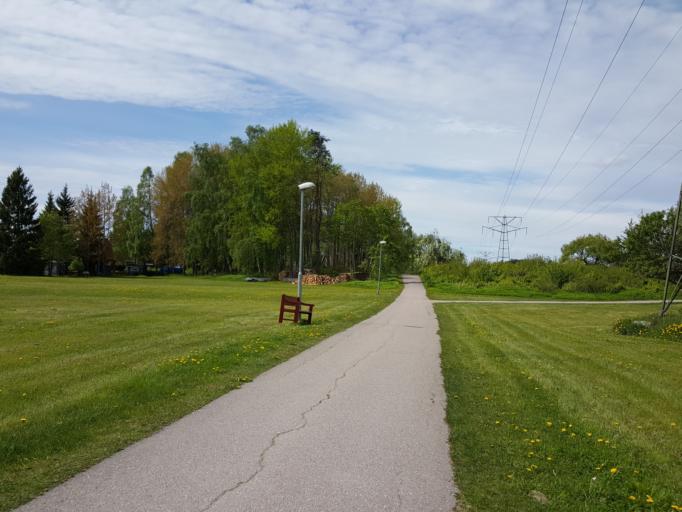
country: SE
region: Uppsala
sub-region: Osthammars Kommun
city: Gimo
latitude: 60.1700
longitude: 18.1834
